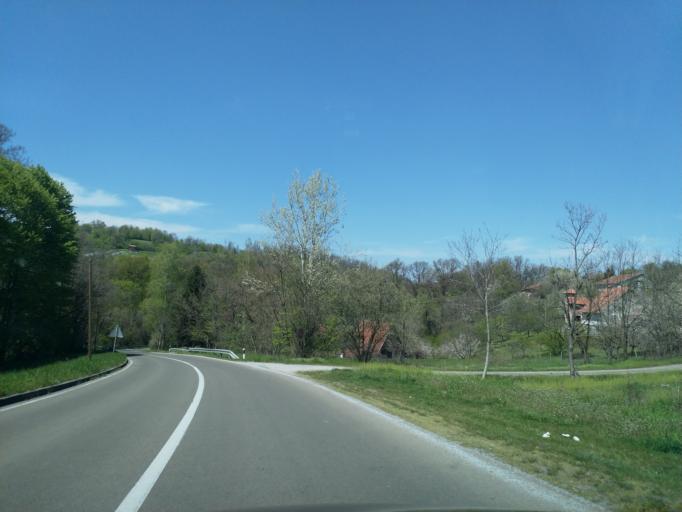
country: RS
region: Central Serbia
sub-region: Belgrade
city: Lazarevac
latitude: 44.3555
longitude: 20.3533
